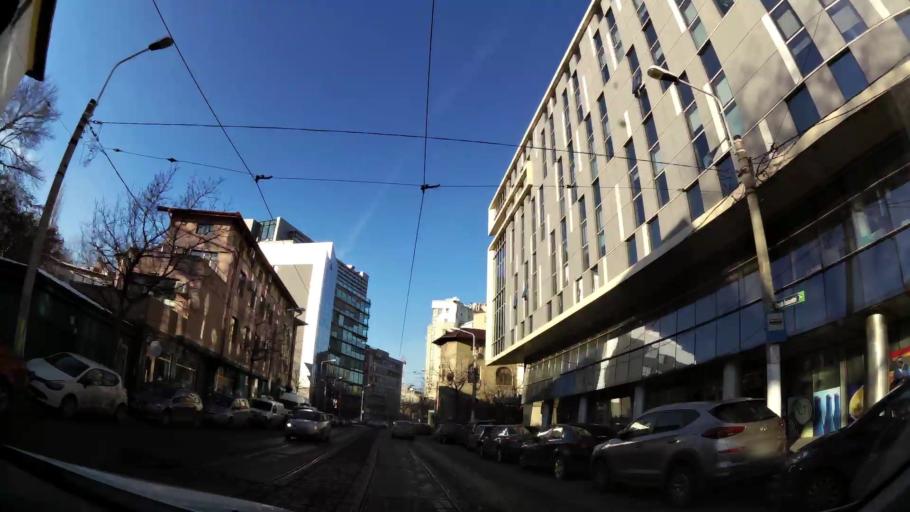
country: RO
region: Bucuresti
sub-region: Municipiul Bucuresti
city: Bucharest
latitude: 44.4393
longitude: 26.1090
